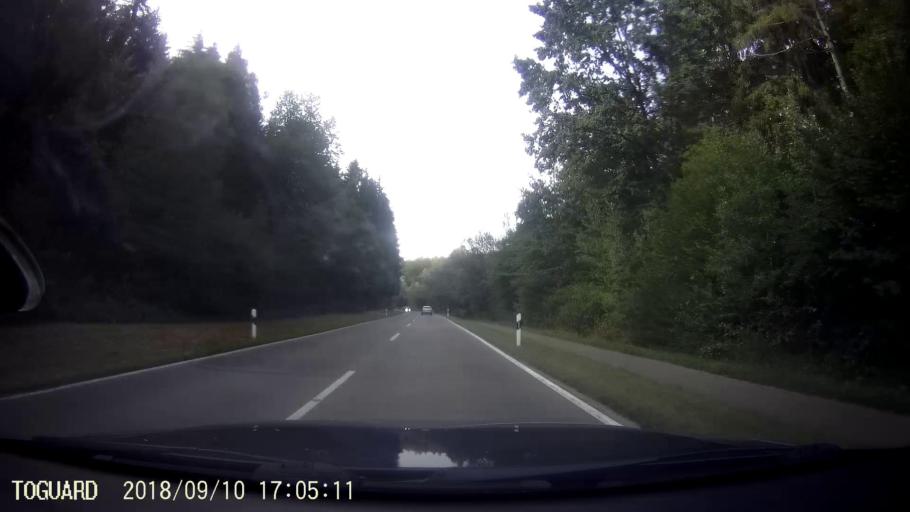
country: DE
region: Baden-Wuerttemberg
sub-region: Freiburg Region
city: Allensbach
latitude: 47.7225
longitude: 9.1298
